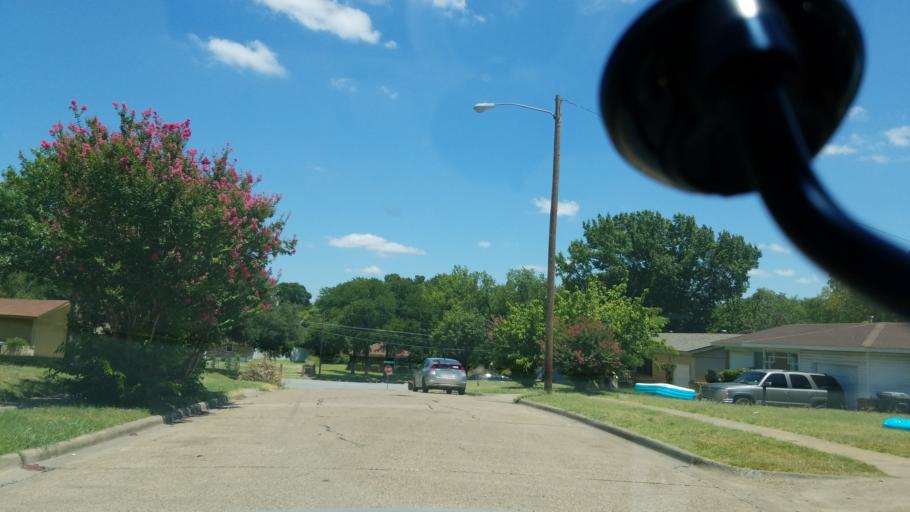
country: US
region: Texas
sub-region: Dallas County
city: Cockrell Hill
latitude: 32.6928
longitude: -96.8157
